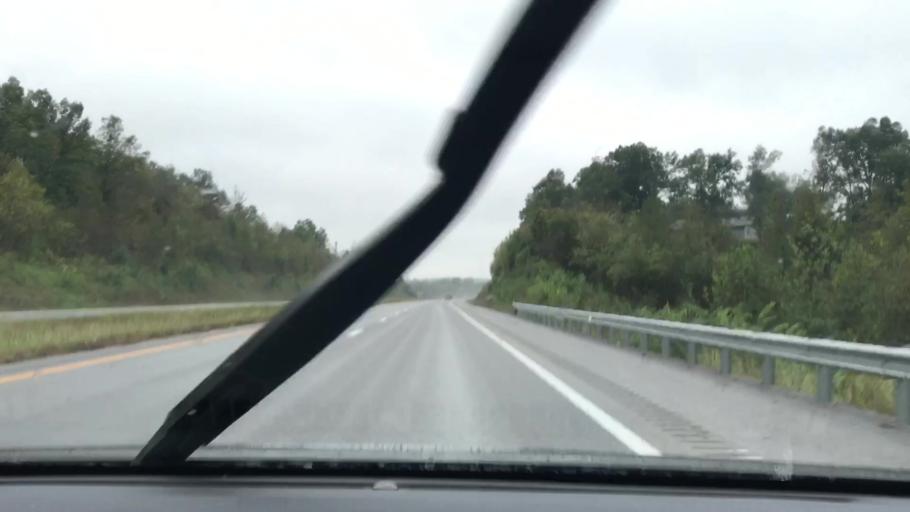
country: US
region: Kentucky
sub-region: Hopkins County
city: Nortonville
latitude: 37.1784
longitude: -87.4470
